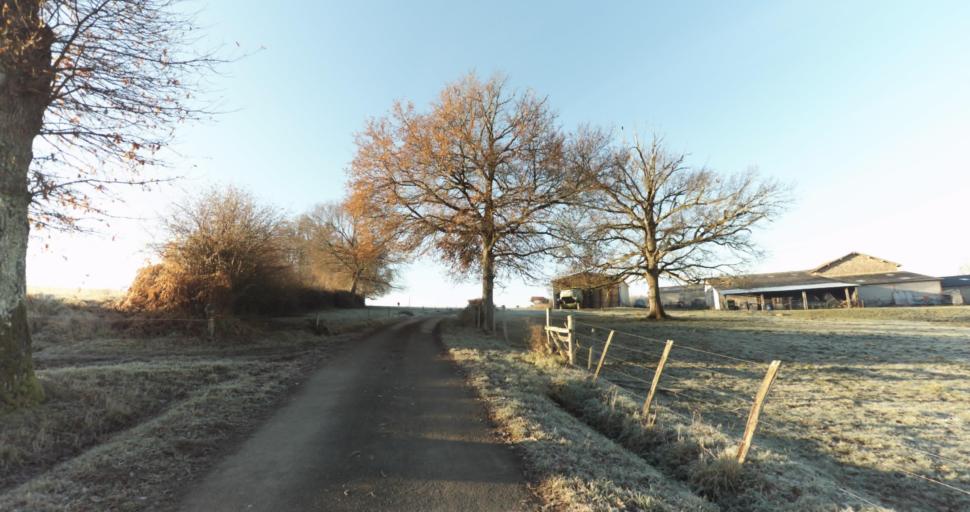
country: FR
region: Limousin
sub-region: Departement de la Haute-Vienne
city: Aixe-sur-Vienne
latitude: 45.8202
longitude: 1.1432
